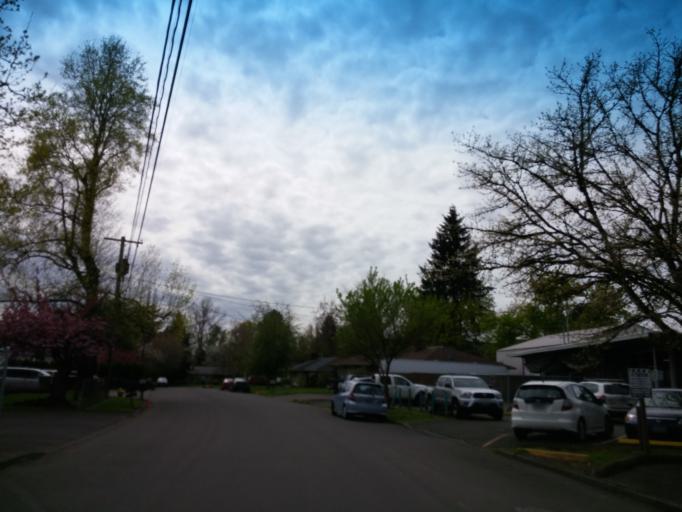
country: US
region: Oregon
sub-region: Washington County
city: Cedar Mill
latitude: 45.5253
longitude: -122.8139
